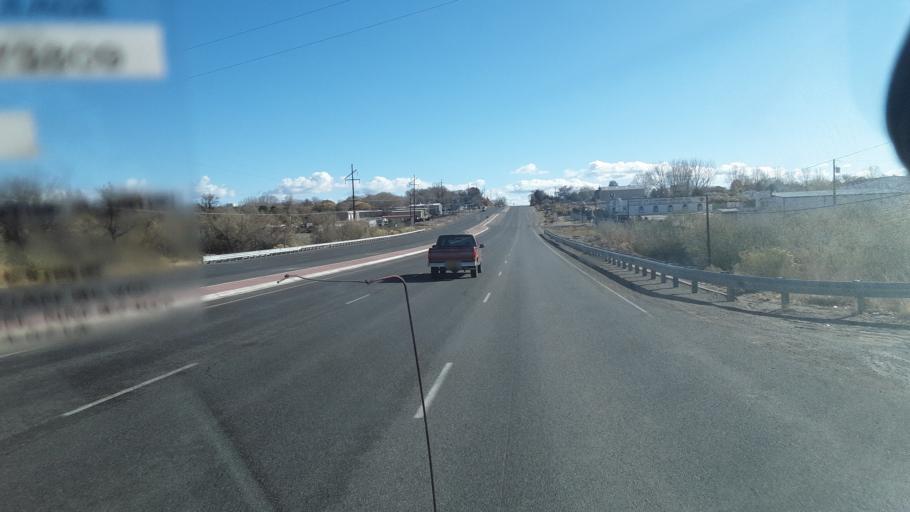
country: US
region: New Mexico
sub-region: San Juan County
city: Lee Acres
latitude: 36.7010
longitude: -108.0648
